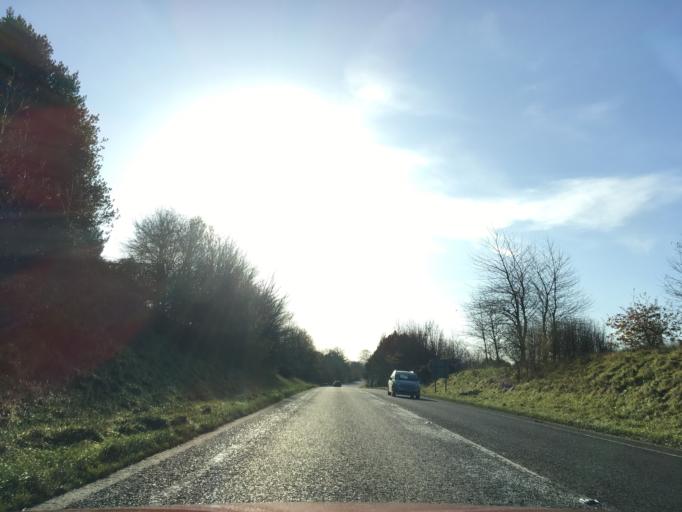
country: GB
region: England
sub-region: Wiltshire
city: Burbage
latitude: 51.3635
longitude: -1.6765
